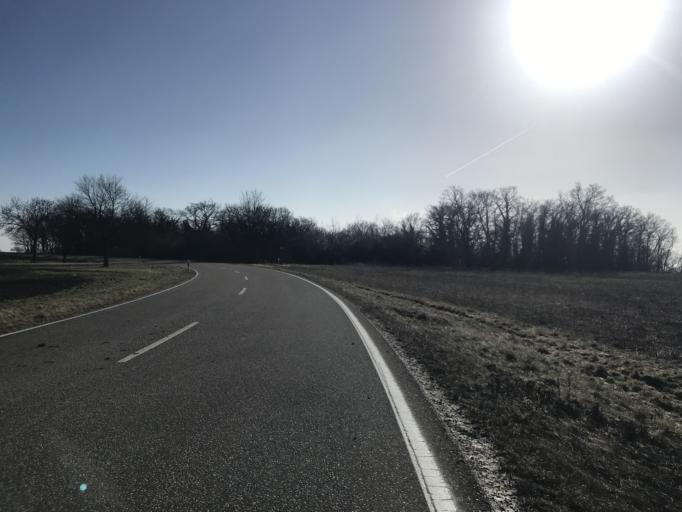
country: DE
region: Rheinland-Pfalz
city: Ober-Hilbersheim
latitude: 49.8845
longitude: 8.0278
